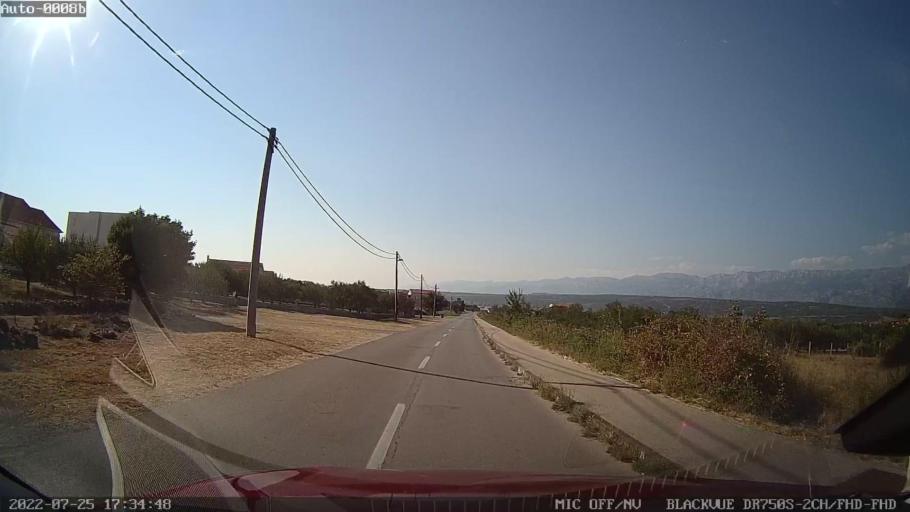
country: HR
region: Zadarska
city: Posedarje
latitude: 44.1860
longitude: 15.4755
